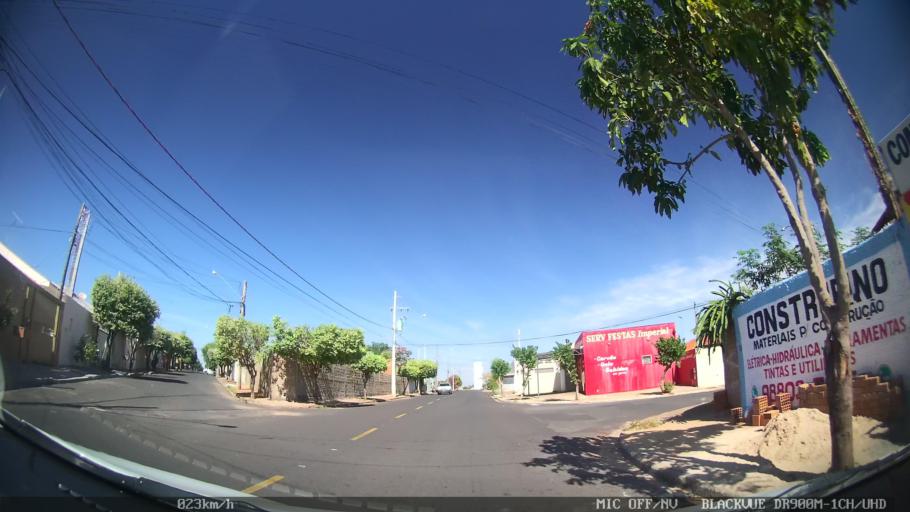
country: BR
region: Sao Paulo
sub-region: Sao Jose Do Rio Preto
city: Sao Jose do Rio Preto
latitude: -20.7677
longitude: -49.4127
